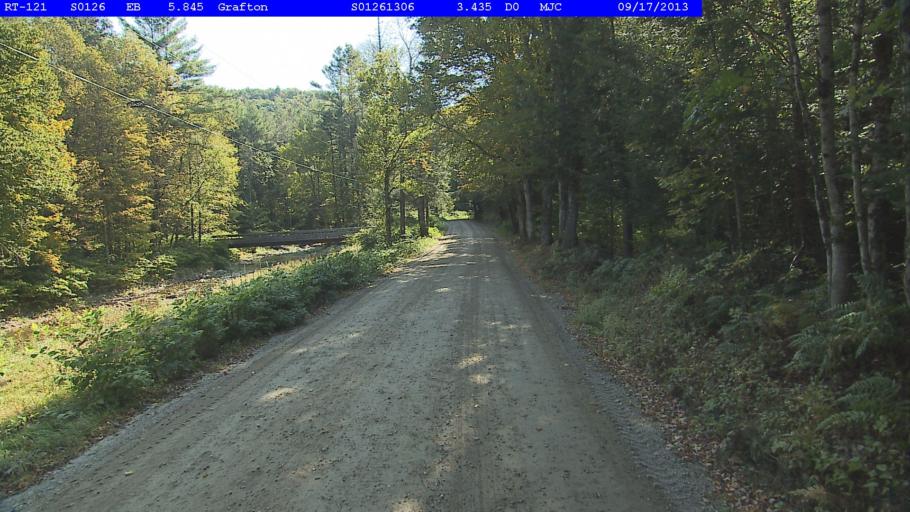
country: US
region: Vermont
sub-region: Windsor County
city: Chester
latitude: 43.1982
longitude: -72.6225
